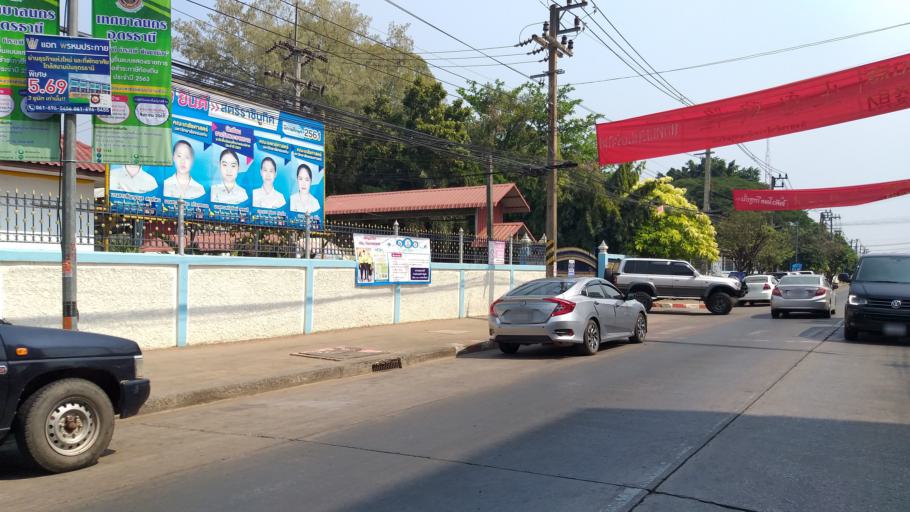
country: TH
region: Changwat Udon Thani
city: Udon Thani
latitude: 17.4072
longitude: 102.7772
